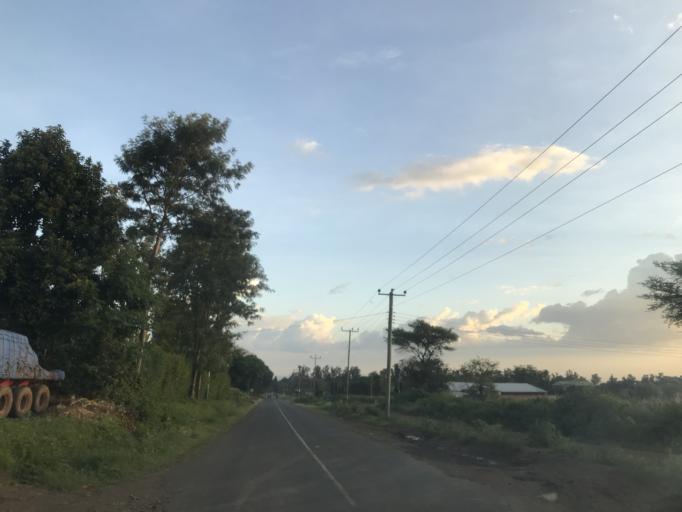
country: TZ
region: Arusha
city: Usa River
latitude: -3.3626
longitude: 36.8681
